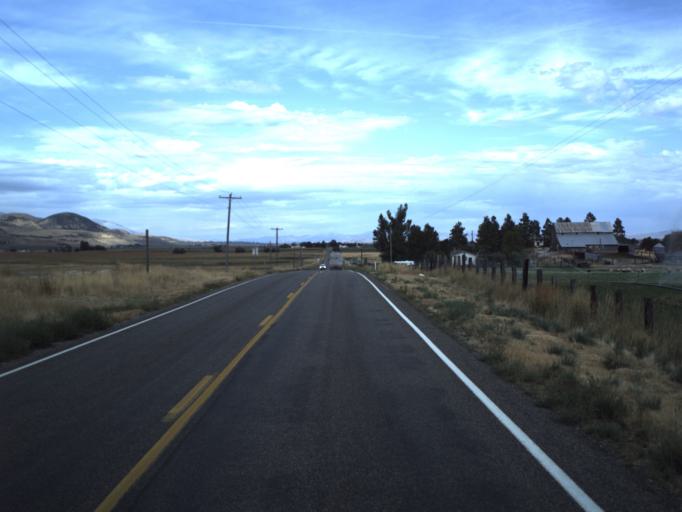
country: US
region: Utah
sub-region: Cache County
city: Lewiston
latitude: 41.9140
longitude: -111.9527
